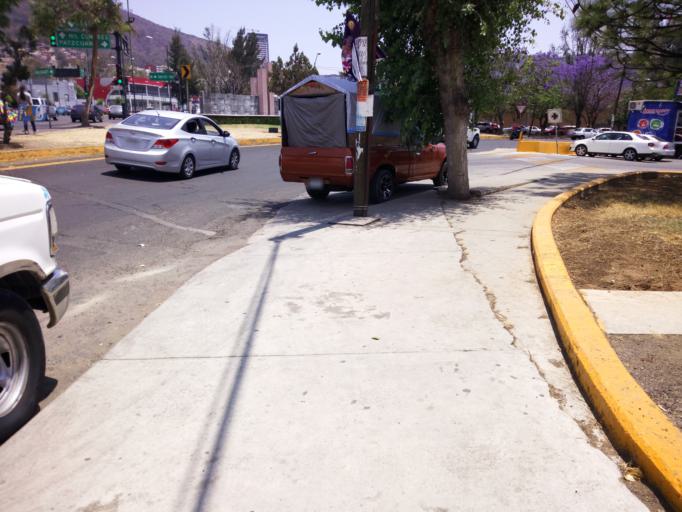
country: MX
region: Michoacan
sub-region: Morelia
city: Puerto de Buenavista (Lazaro Cardenas)
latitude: 19.6946
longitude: -101.1501
